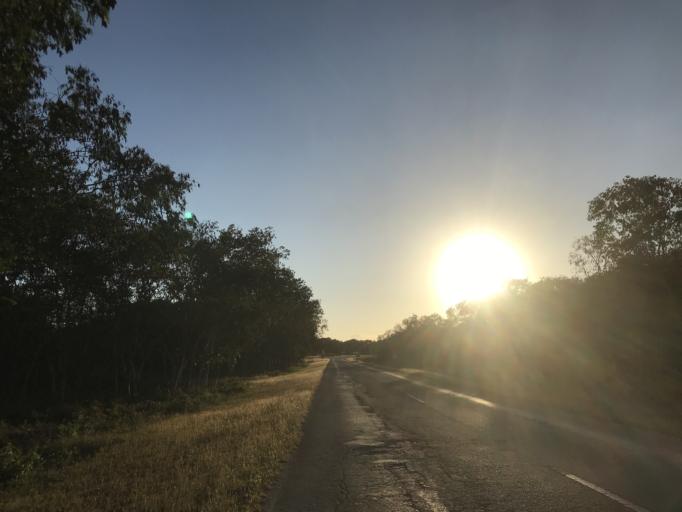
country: CU
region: Cienfuegos
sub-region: Municipio de Aguada de Pasajeros
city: Aguada de Pasajeros
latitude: 22.0685
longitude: -81.0397
